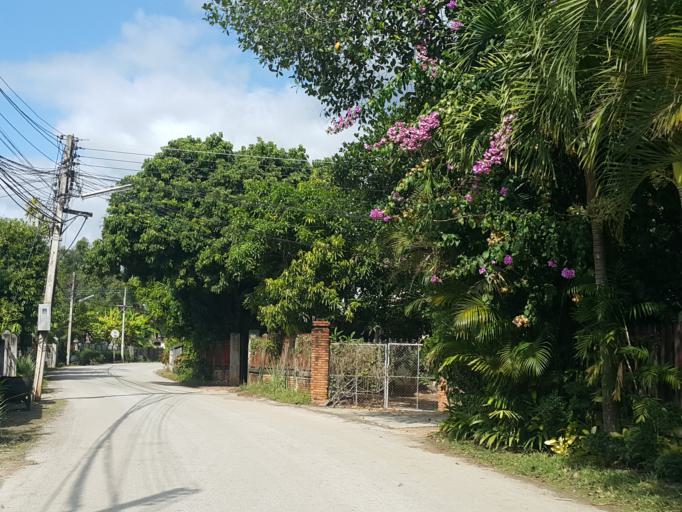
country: TH
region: Lampang
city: Hang Chat
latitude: 18.3381
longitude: 99.3571
